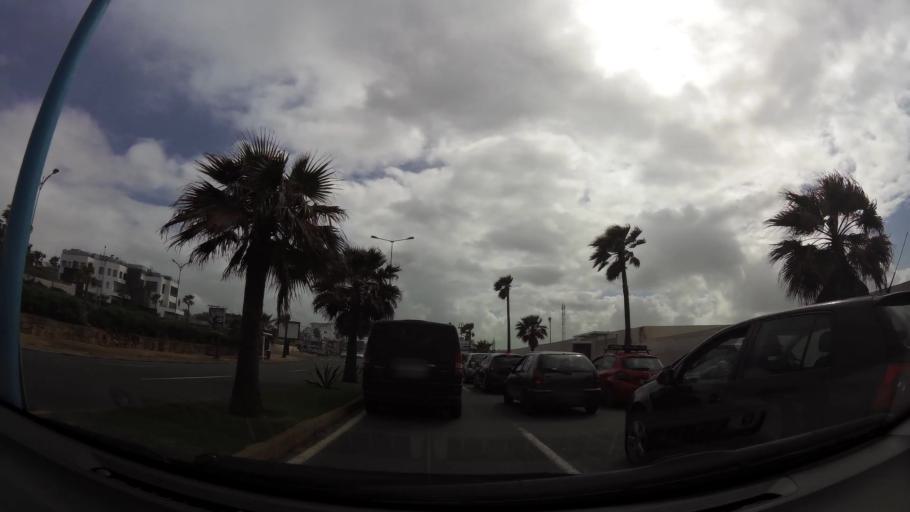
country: MA
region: Grand Casablanca
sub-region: Casablanca
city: Casablanca
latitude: 33.6033
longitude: -7.6600
